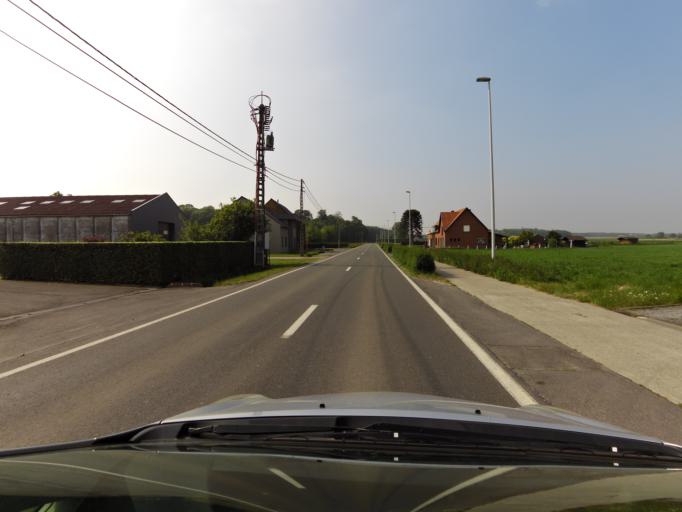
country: BE
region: Flanders
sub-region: Provincie West-Vlaanderen
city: Poperinge
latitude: 50.8769
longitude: 2.7050
